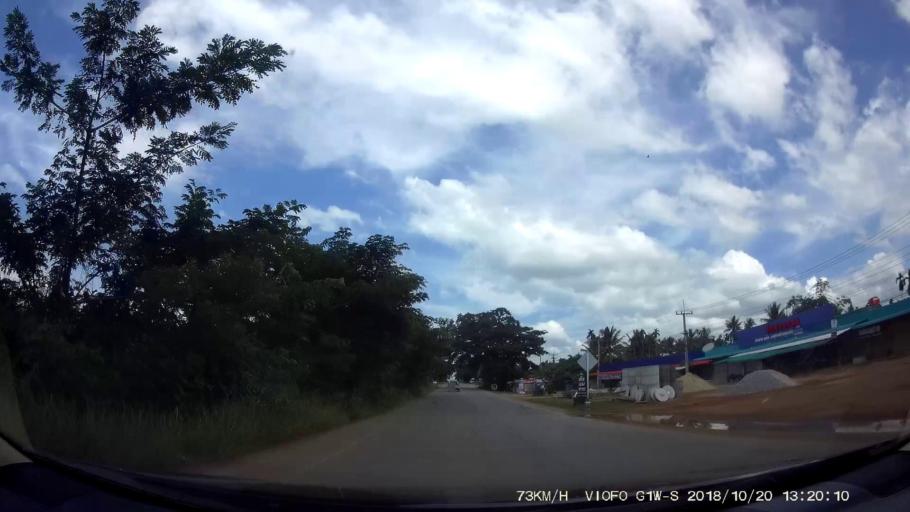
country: TH
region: Chaiyaphum
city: Khon San
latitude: 16.5455
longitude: 101.9028
